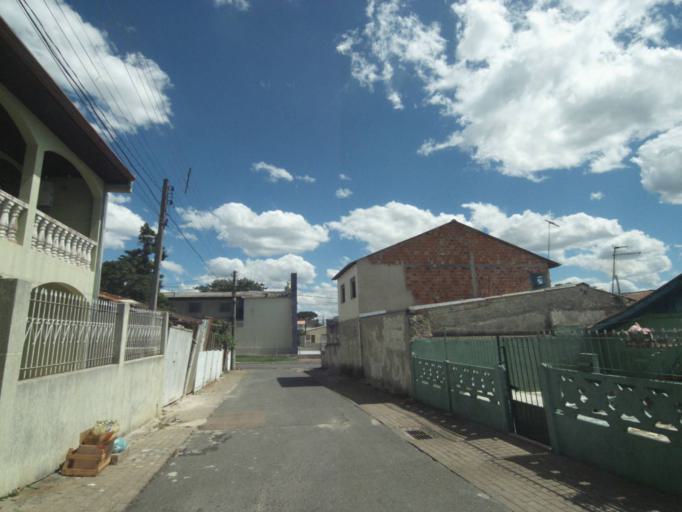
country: BR
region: Parana
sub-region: Curitiba
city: Curitiba
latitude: -25.5100
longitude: -49.3246
